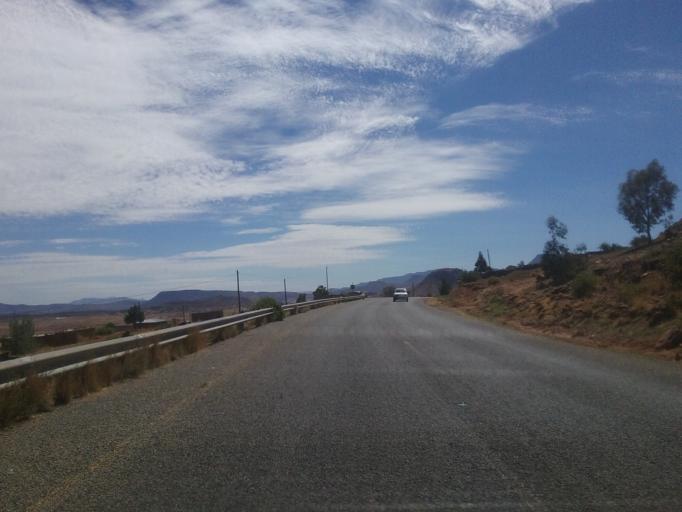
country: LS
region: Mohale's Hoek District
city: Mohale's Hoek
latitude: -30.1887
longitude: 27.4173
